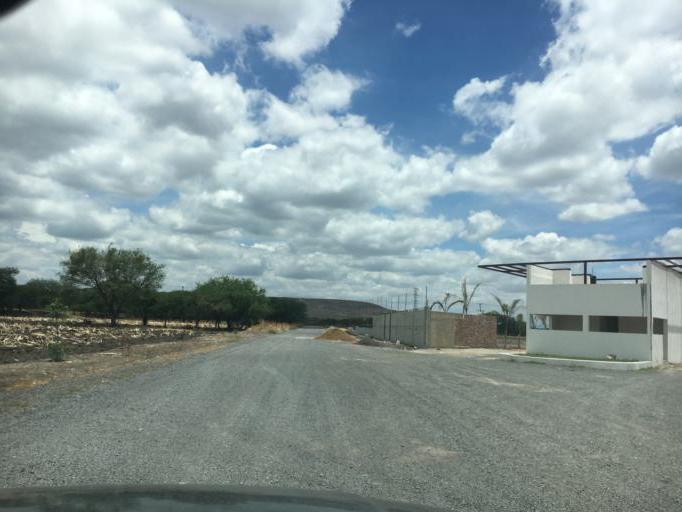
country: MX
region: Guanajuato
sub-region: Leon
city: Plan Guanajuato (La Sandia)
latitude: 20.9161
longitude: -101.7486
